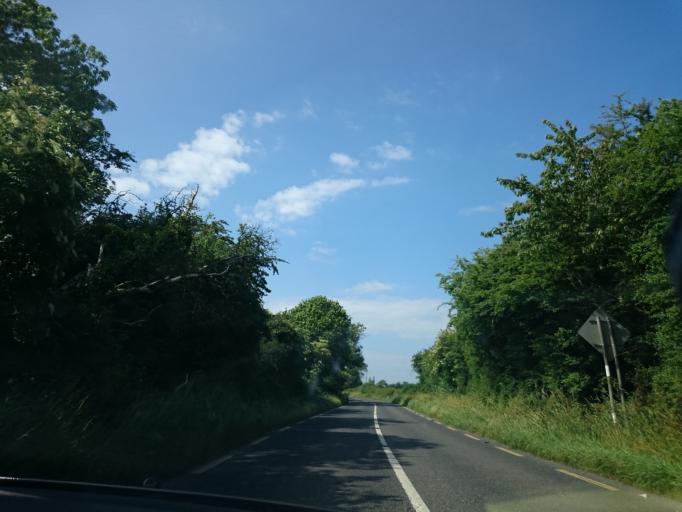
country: IE
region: Leinster
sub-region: Kilkenny
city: Thomastown
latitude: 52.5518
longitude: -7.2275
